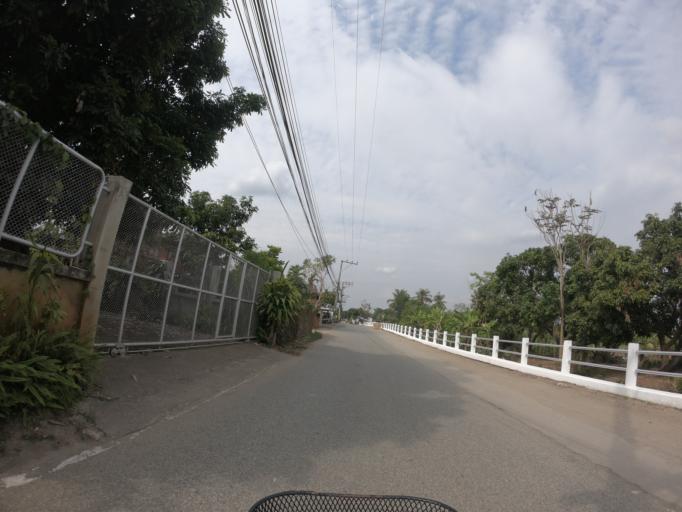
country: TH
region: Chiang Mai
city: Saraphi
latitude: 18.7369
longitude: 99.0247
